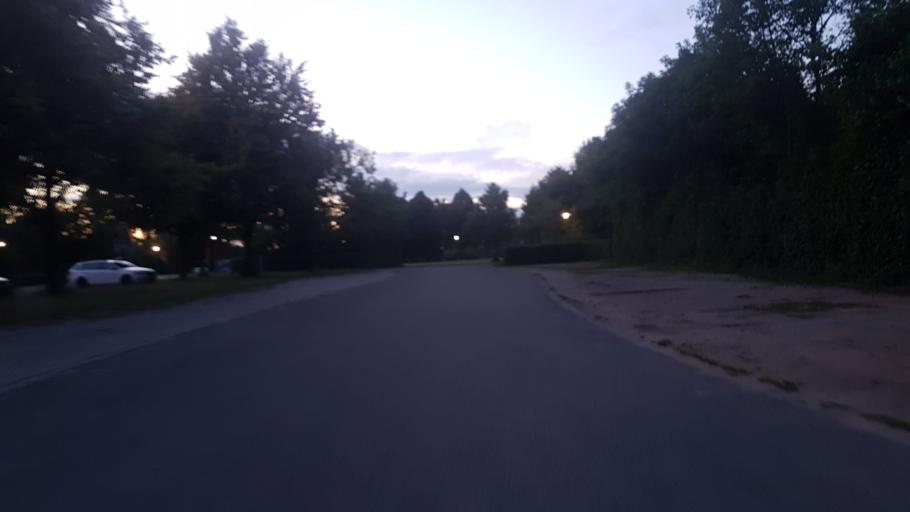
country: DE
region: Bavaria
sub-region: Regierungsbezirk Mittelfranken
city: Gunzenhausen
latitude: 49.1251
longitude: 10.7411
